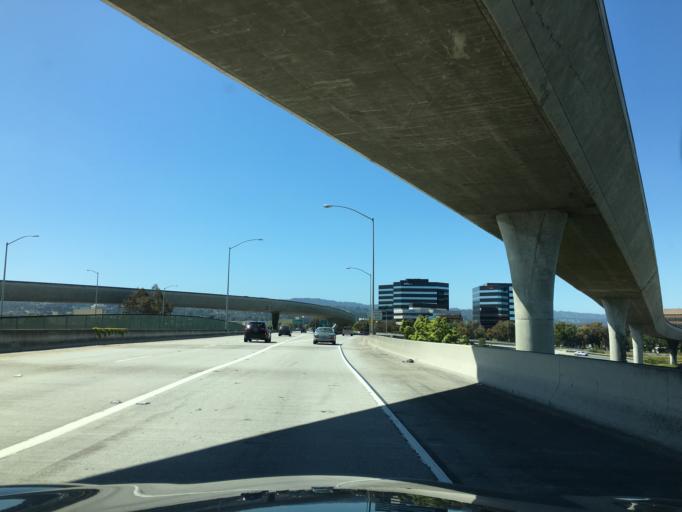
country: US
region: California
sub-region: San Mateo County
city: Foster City
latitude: 37.5536
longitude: -122.2952
